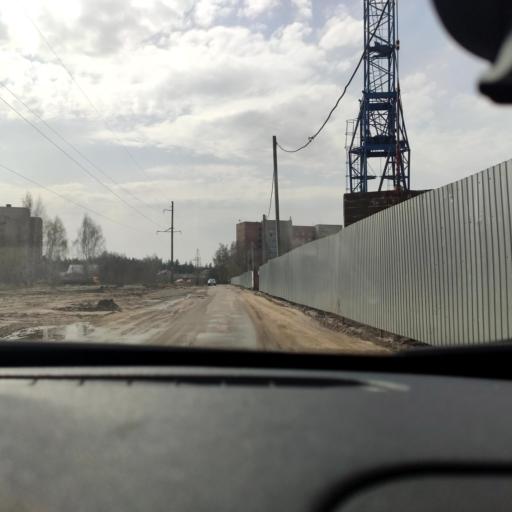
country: RU
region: Voronezj
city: Podgornoye
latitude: 51.7589
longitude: 39.1751
